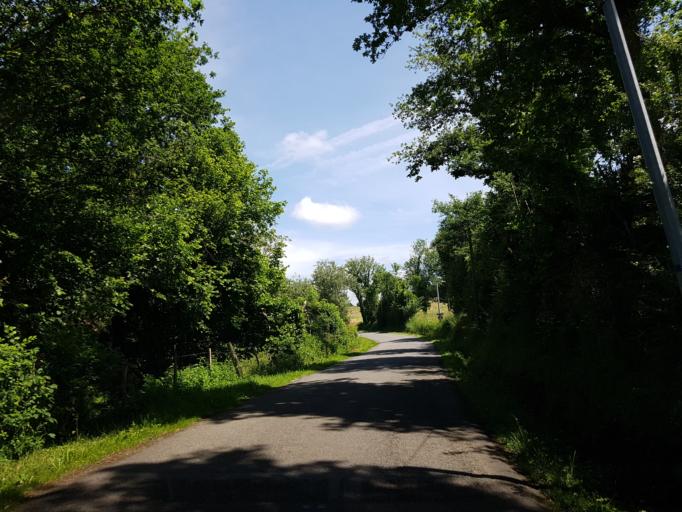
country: FR
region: Poitou-Charentes
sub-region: Departement de la Charente
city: Chabanais
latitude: 45.8908
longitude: 0.7426
